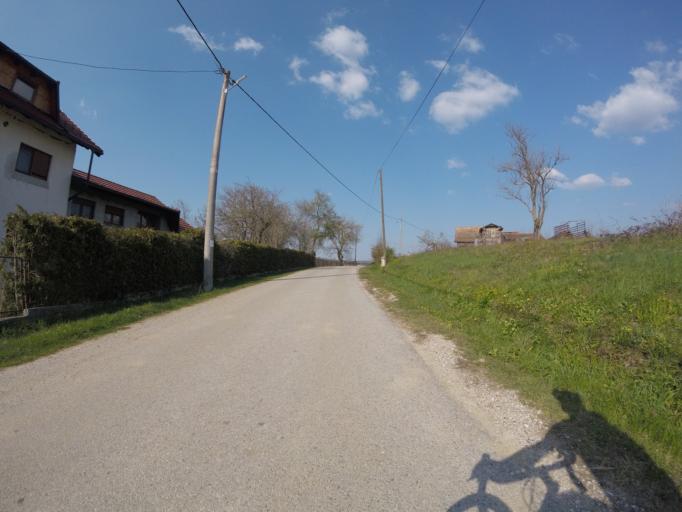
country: HR
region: Sisacko-Moslavacka
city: Glina
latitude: 45.5006
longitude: 15.9941
